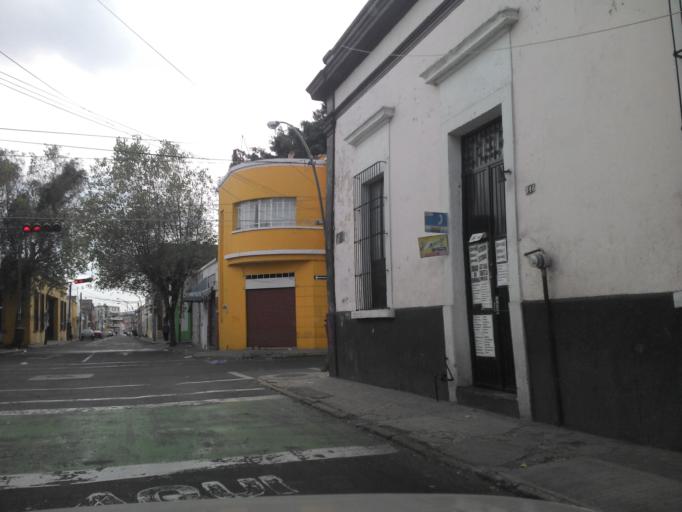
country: MX
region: Jalisco
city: Guadalajara
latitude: 20.6716
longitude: -103.3525
